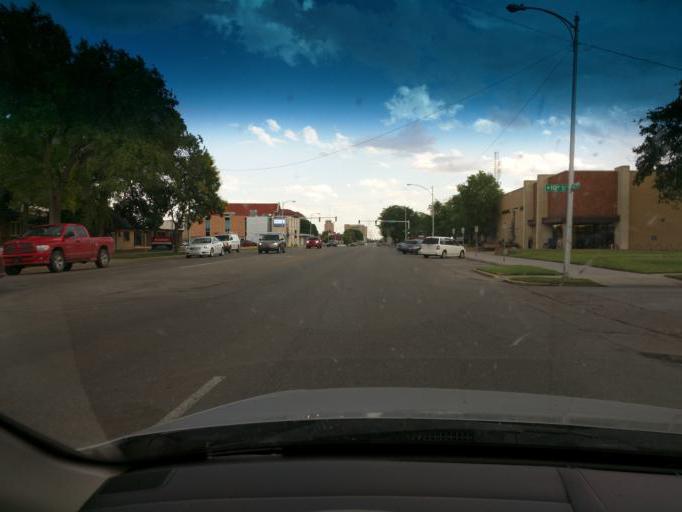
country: US
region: Kansas
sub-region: Reno County
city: Hutchinson
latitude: 38.0640
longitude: -97.9319
